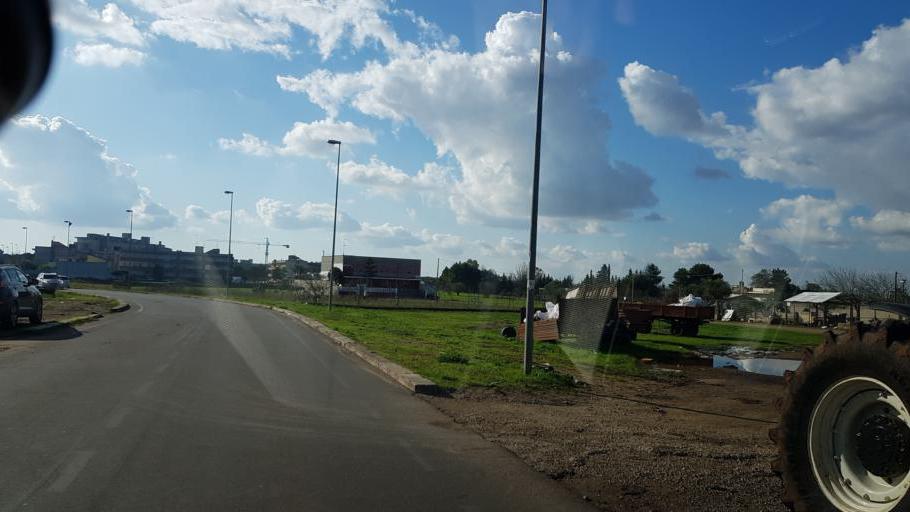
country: IT
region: Apulia
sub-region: Provincia di Lecce
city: Campi Salentina
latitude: 40.4063
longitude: 18.0189
